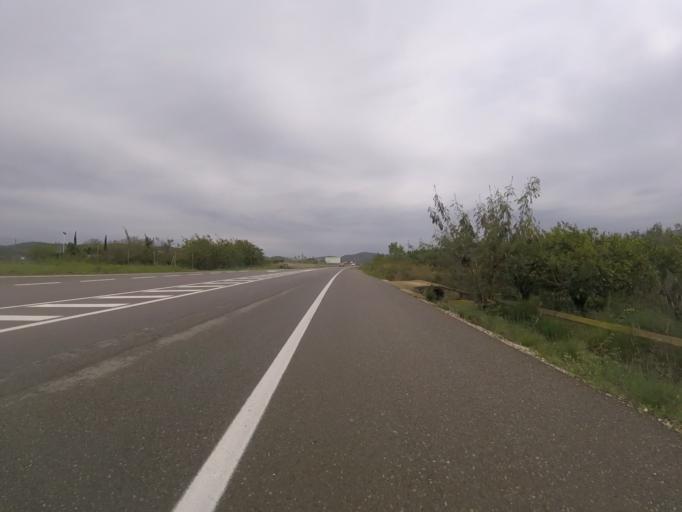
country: ES
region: Valencia
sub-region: Provincia de Castello
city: Alcoceber
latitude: 40.2571
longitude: 0.2446
